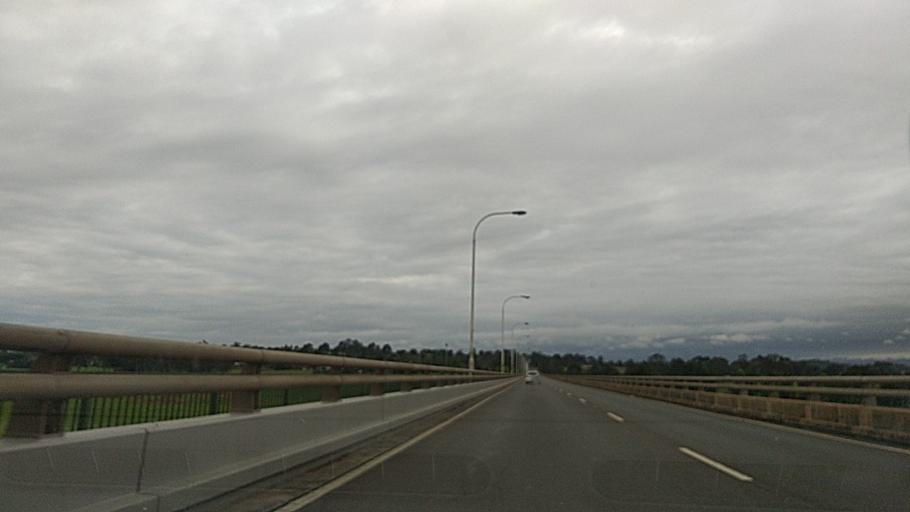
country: AU
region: New South Wales
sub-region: Camden
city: Camden South
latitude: -34.0707
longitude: 150.7013
